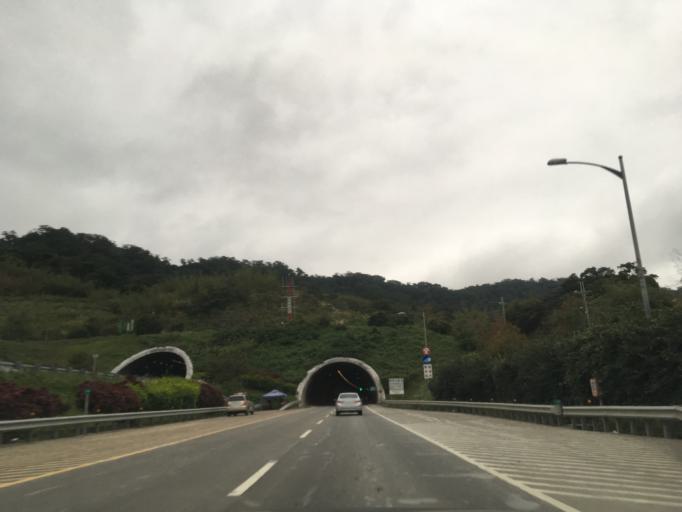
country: TW
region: Taipei
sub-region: Taipei
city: Banqiao
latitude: 25.1116
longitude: 121.4222
